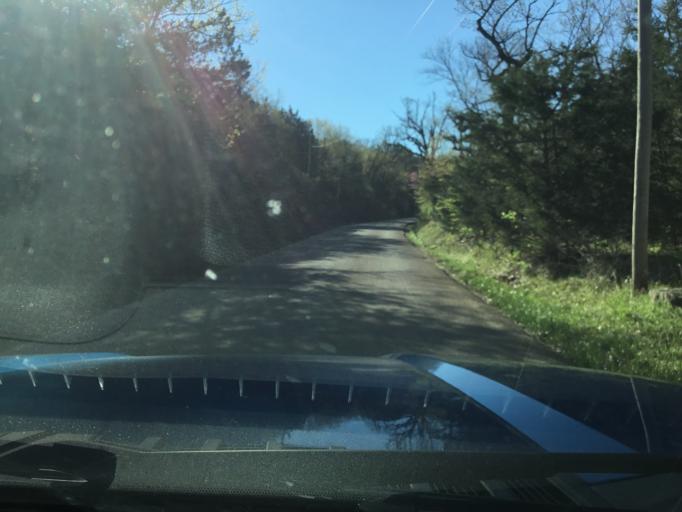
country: US
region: Kansas
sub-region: Douglas County
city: Lawrence
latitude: 38.9917
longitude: -95.2976
